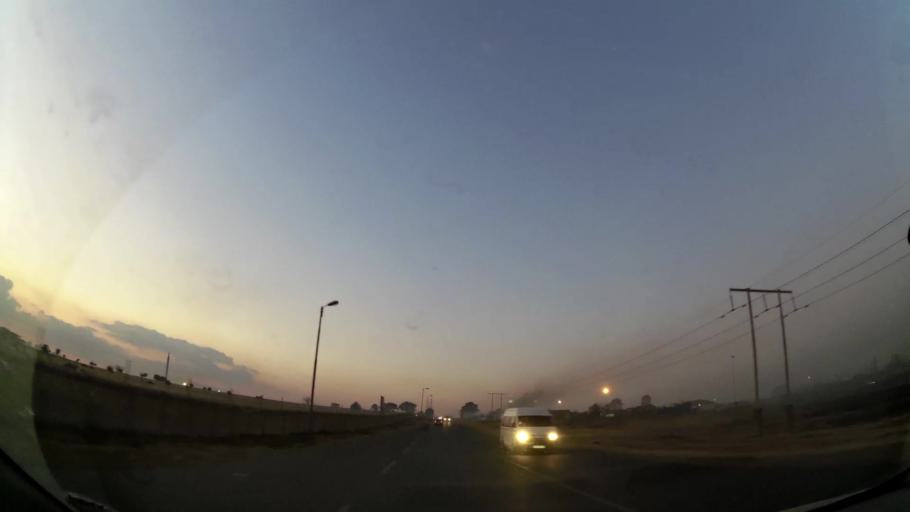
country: ZA
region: Gauteng
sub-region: Ekurhuleni Metropolitan Municipality
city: Springs
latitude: -26.2983
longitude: 28.3819
